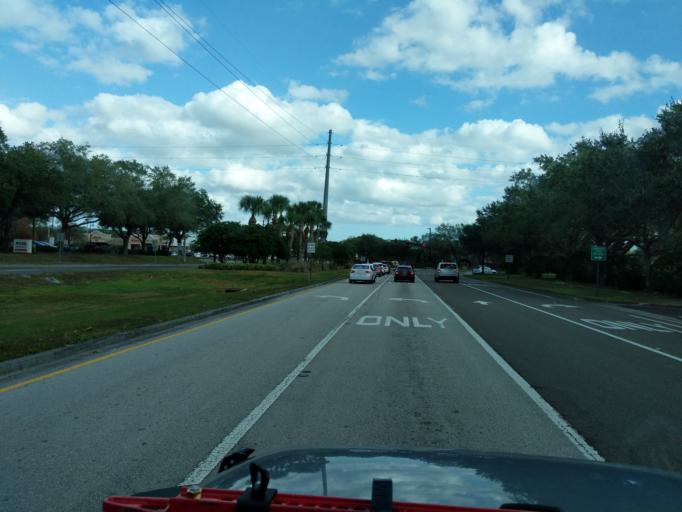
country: US
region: Florida
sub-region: Seminole County
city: Oviedo
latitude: 28.6559
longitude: -81.1804
